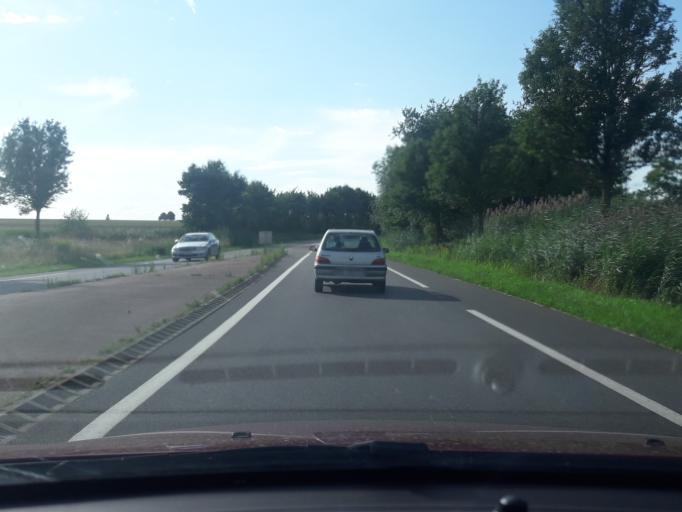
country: FR
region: Alsace
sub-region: Departement du Bas-Rhin
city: Ohlungen
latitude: 48.7851
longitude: 7.6719
